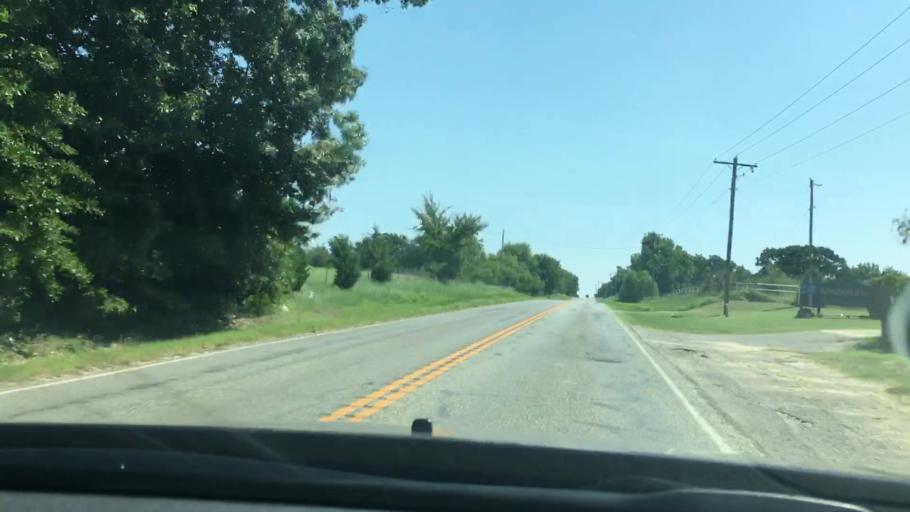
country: US
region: Oklahoma
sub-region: Johnston County
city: Tishomingo
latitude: 34.2377
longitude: -96.6059
